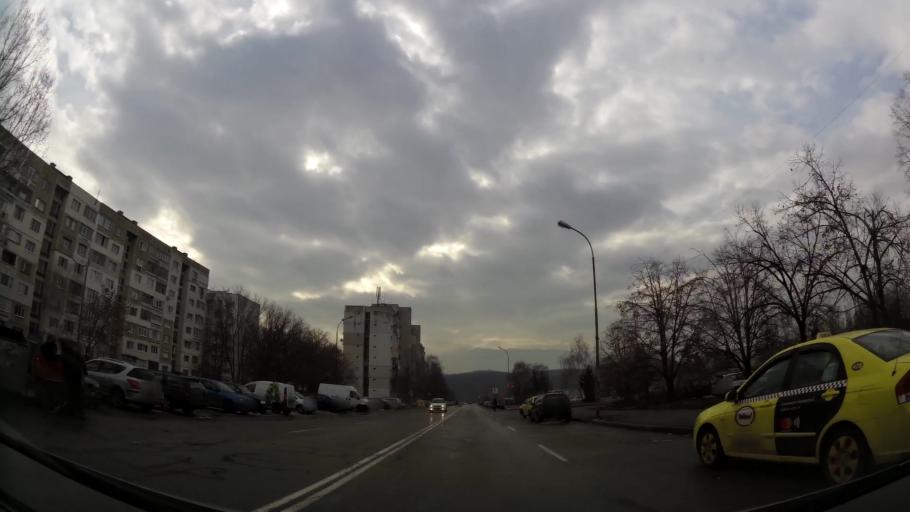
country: BG
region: Sofia-Capital
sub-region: Stolichna Obshtina
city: Sofia
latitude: 42.7126
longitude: 23.2586
